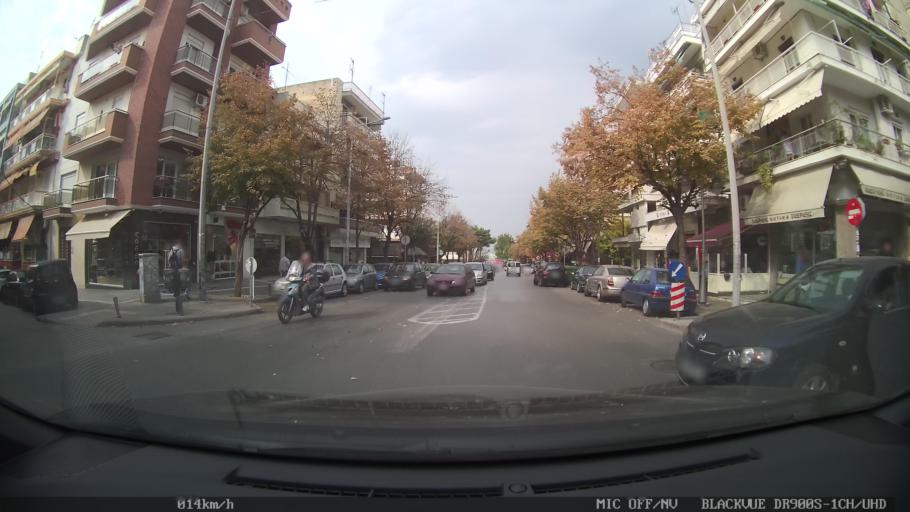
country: GR
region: Central Macedonia
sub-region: Nomos Thessalonikis
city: Triandria
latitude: 40.6154
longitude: 22.9756
